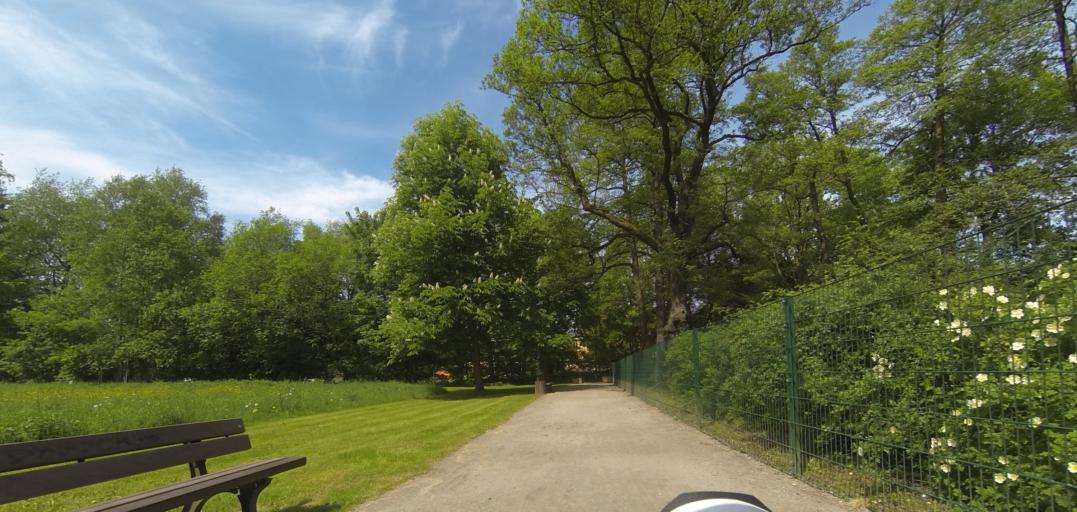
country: DE
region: Saxony
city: Arnsdorf
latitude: 51.0923
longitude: 13.9905
